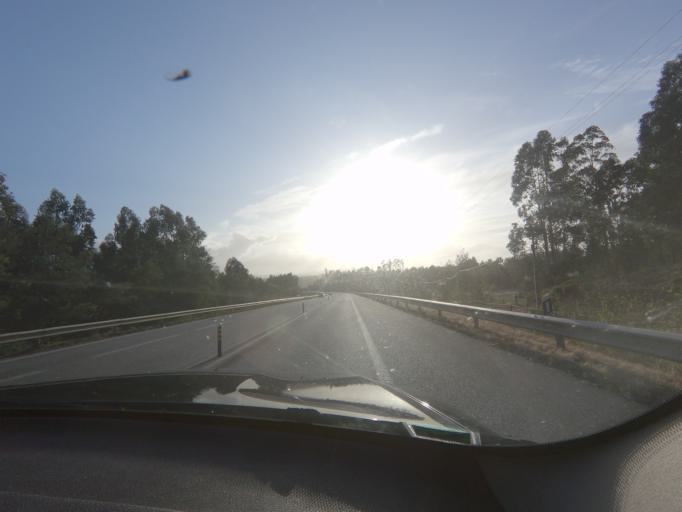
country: PT
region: Viseu
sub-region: Santa Comba Dao
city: Santa Comba Dao
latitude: 40.3503
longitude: -8.1650
